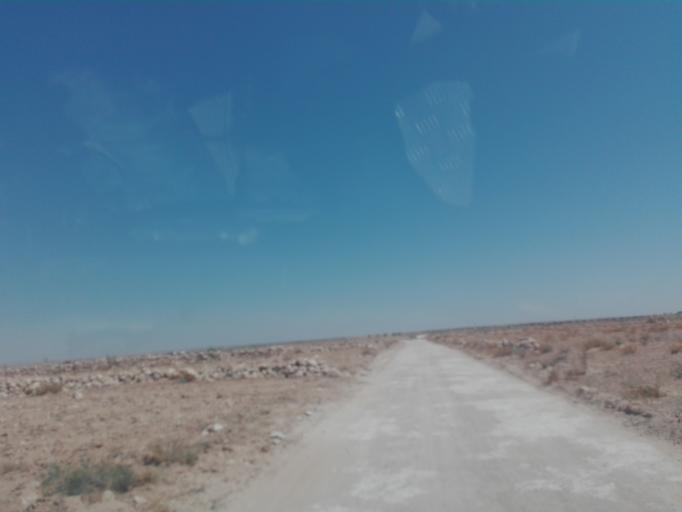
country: TN
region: Safaqis
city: Skhira
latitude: 34.3978
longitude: 9.9284
